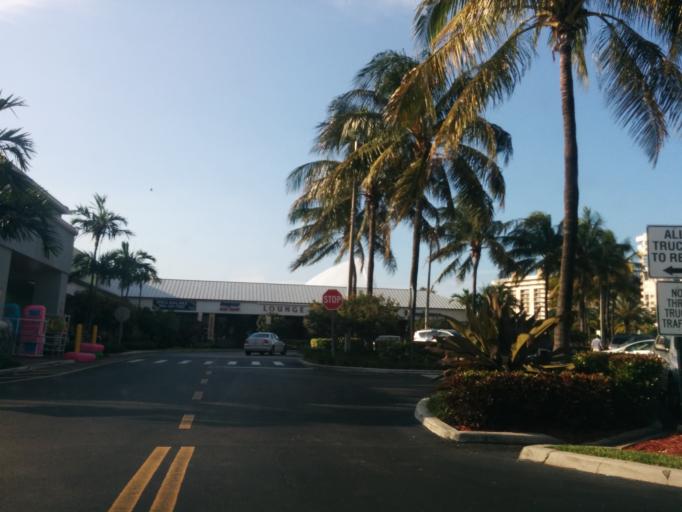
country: US
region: Florida
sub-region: Broward County
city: Lauderdale-by-the-Sea
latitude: 26.1971
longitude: -80.0968
